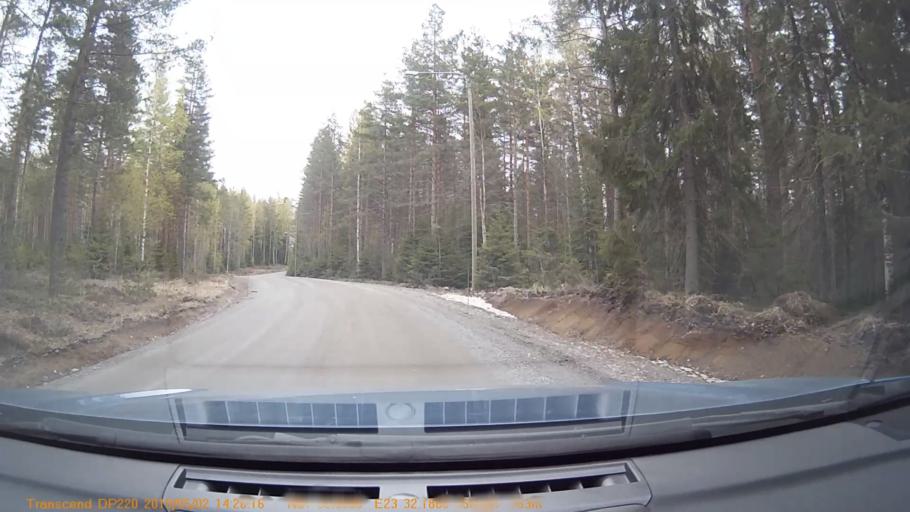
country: FI
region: Pirkanmaa
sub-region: Tampere
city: Yloejaervi
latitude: 61.5509
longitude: 23.5362
